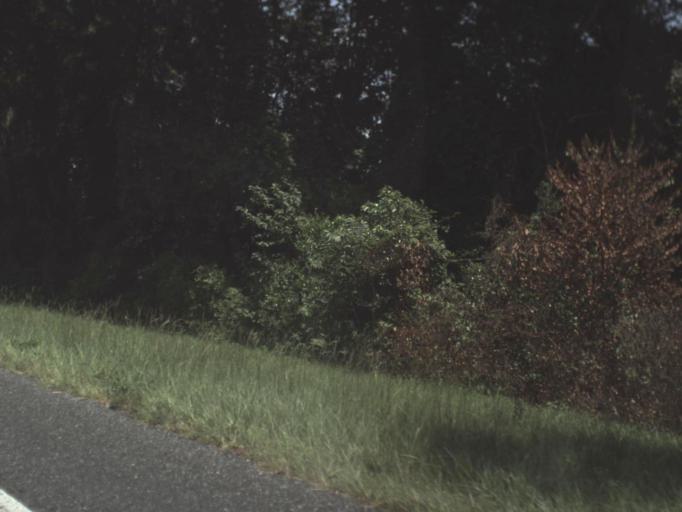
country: US
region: Florida
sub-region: Levy County
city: Chiefland
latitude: 29.5072
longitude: -82.8256
